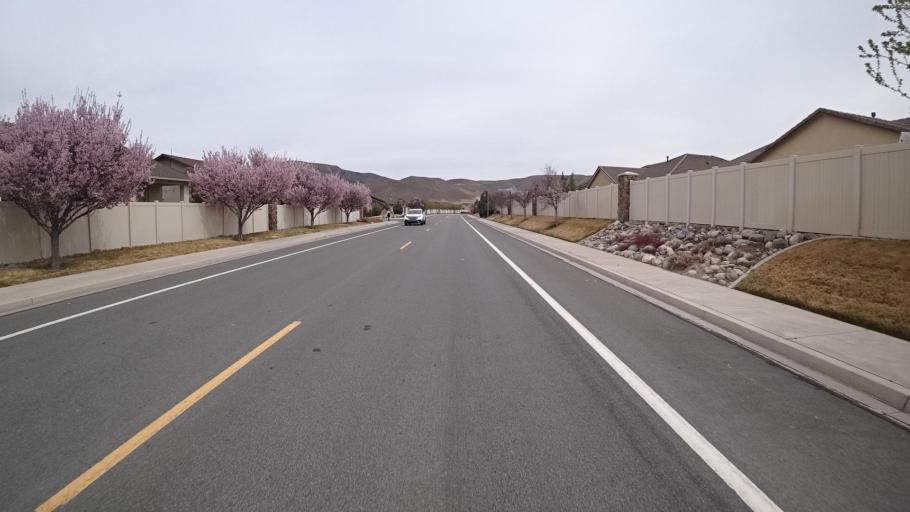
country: US
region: Nevada
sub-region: Washoe County
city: Sparks
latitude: 39.4375
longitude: -119.7259
